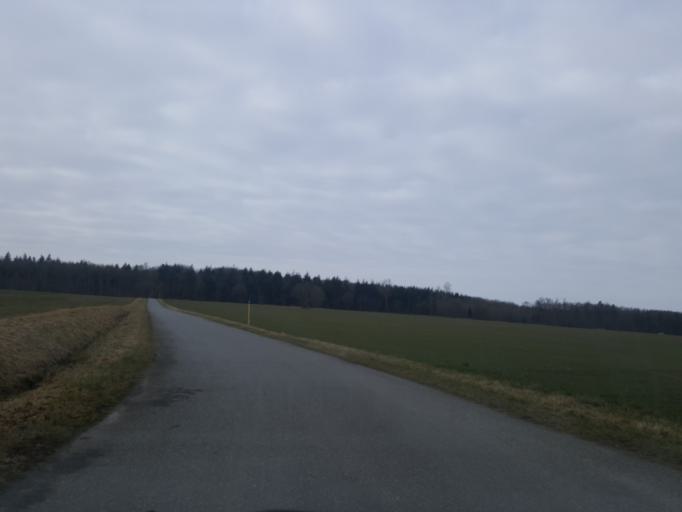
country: DK
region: Zealand
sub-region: Vordingborg Kommune
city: Neder Vindinge
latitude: 55.0416
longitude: 11.8203
